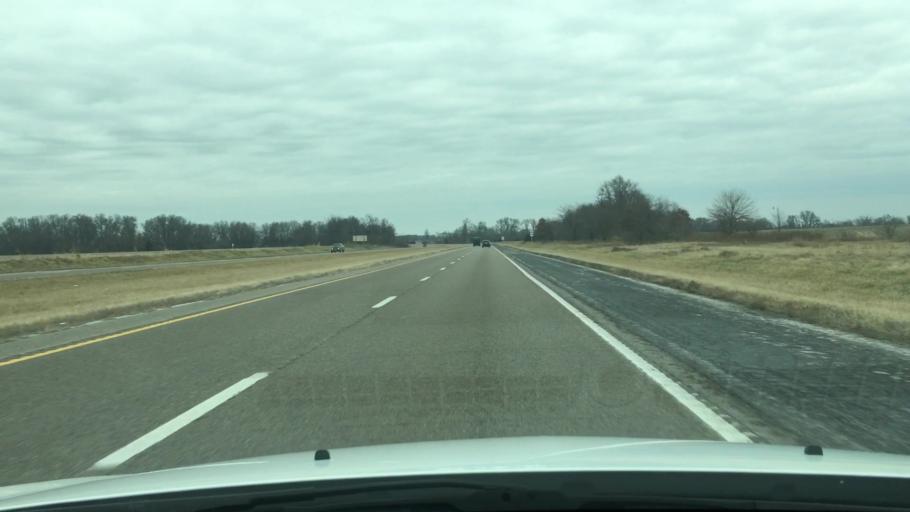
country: US
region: Missouri
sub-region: Audrain County
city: Mexico
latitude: 39.0232
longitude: -91.8856
